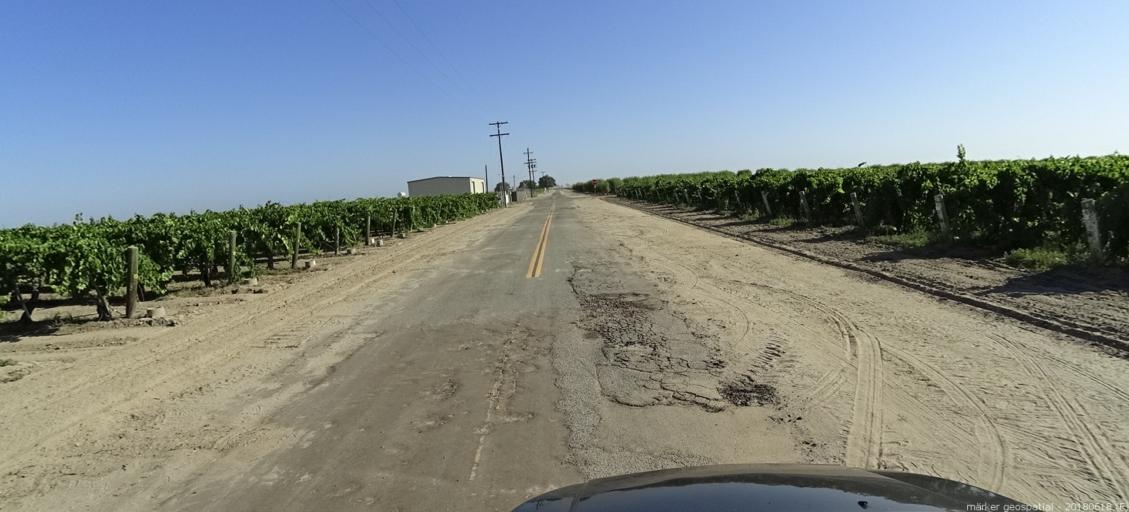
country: US
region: California
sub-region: Fresno County
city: Biola
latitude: 36.8287
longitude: -120.1059
